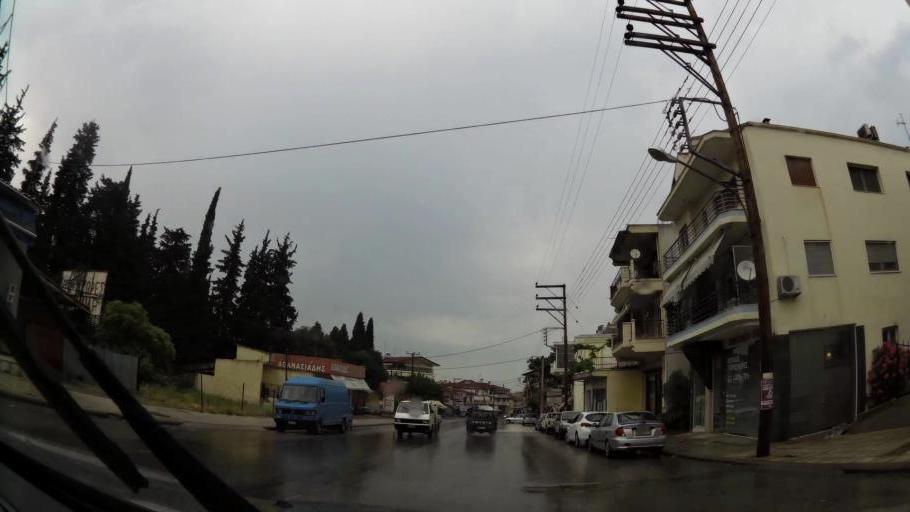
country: GR
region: Central Macedonia
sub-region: Nomos Imathias
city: Veroia
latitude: 40.5324
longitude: 22.2012
